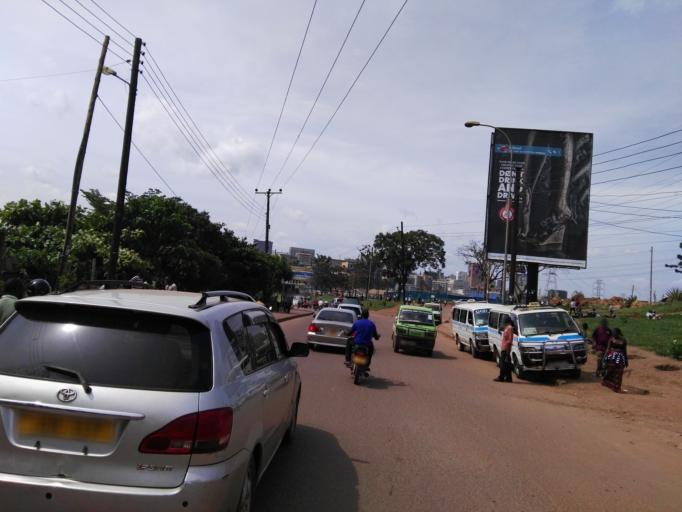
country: UG
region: Central Region
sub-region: Kampala District
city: Kampala
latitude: 0.3033
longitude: 32.5769
